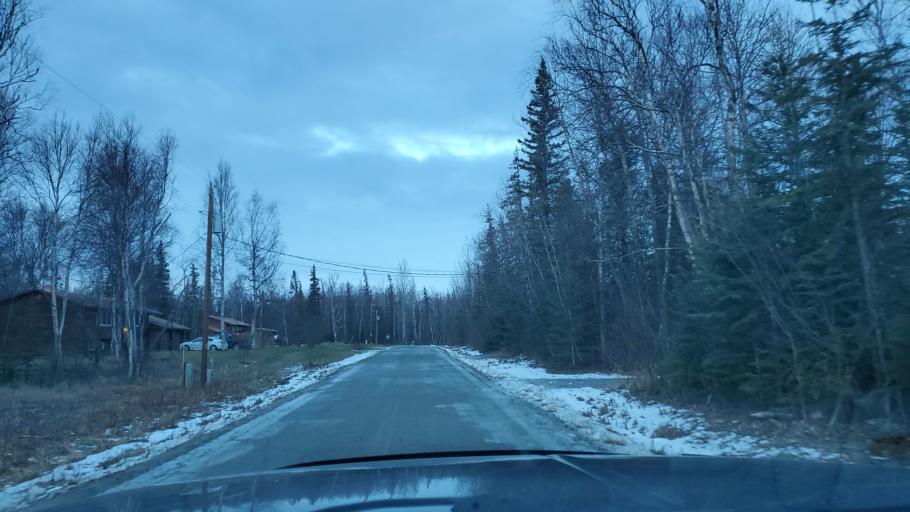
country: US
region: Alaska
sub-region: Matanuska-Susitna Borough
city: Wasilla
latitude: 61.5902
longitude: -149.4134
